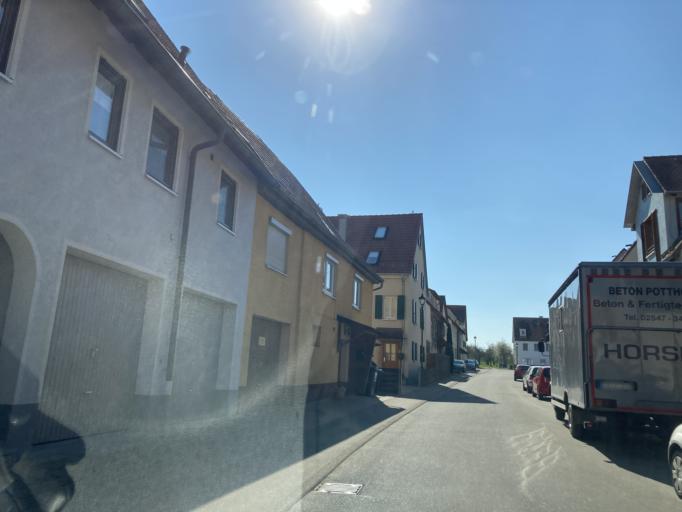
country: DE
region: Baden-Wuerttemberg
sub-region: Regierungsbezirk Stuttgart
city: Hildrizhausen
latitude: 48.5710
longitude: 8.9567
